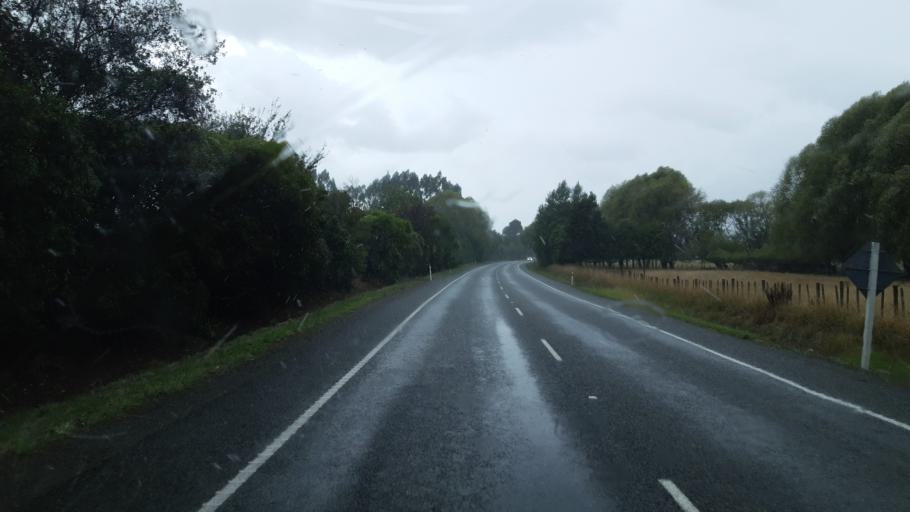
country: NZ
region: Tasman
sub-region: Tasman District
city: Brightwater
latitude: -41.3822
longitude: 173.0853
